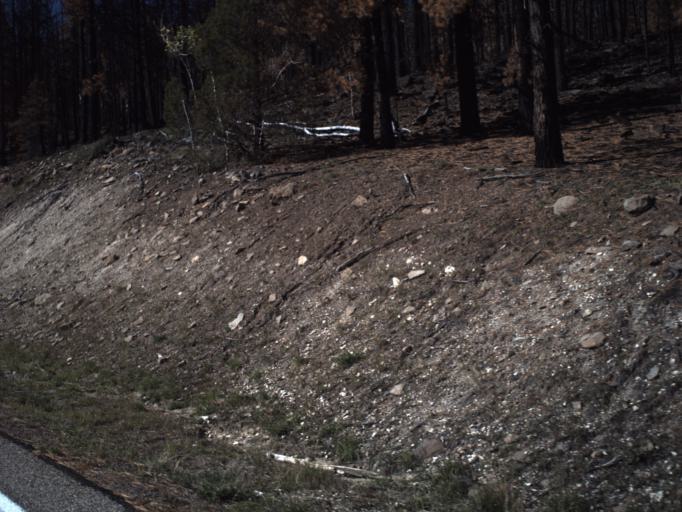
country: US
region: Utah
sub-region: Iron County
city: Parowan
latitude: 37.6516
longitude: -112.6968
